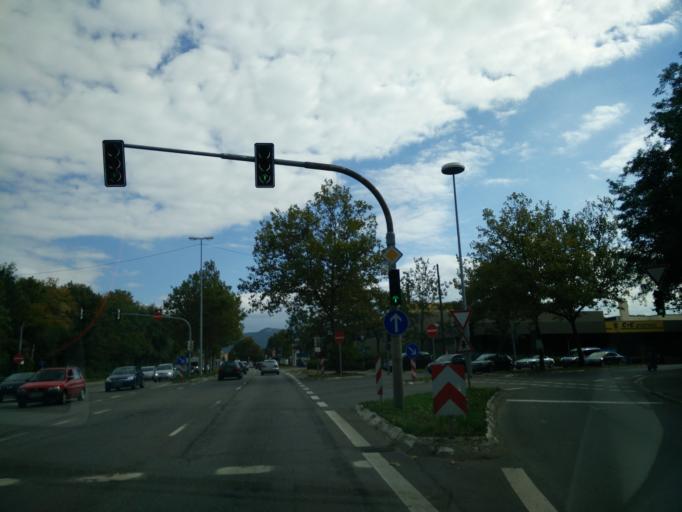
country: DE
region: Baden-Wuerttemberg
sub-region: Tuebingen Region
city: Pfullingen
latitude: 48.4844
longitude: 9.2236
